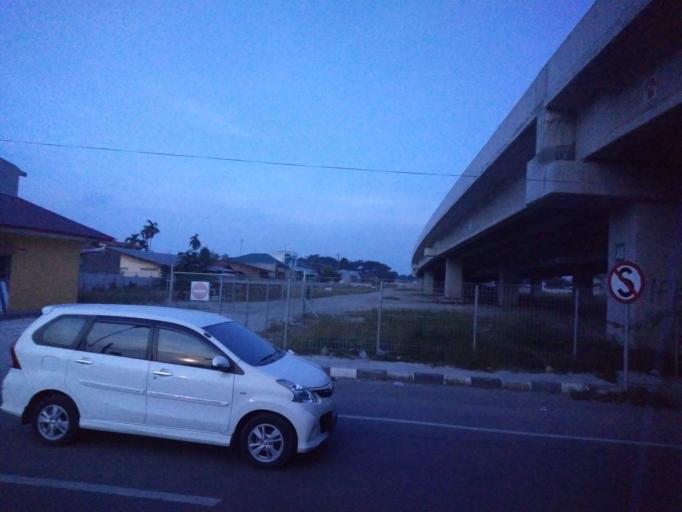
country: ID
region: North Sumatra
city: Medan
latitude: 3.6494
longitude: 98.6572
